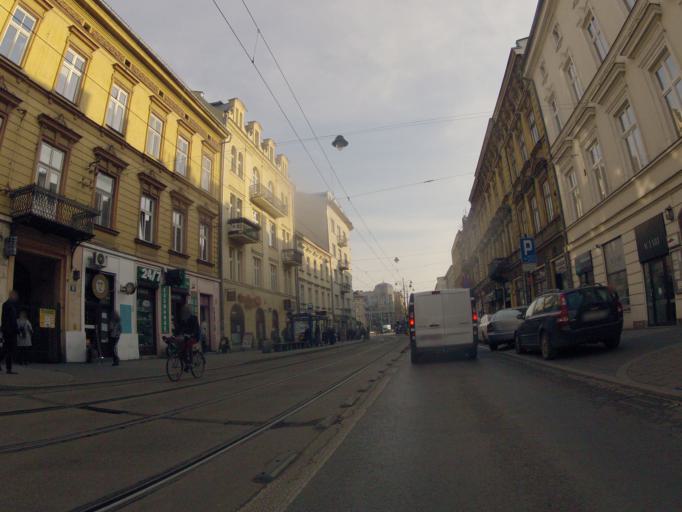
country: PL
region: Lesser Poland Voivodeship
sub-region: Krakow
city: Krakow
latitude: 50.0576
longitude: 19.9443
